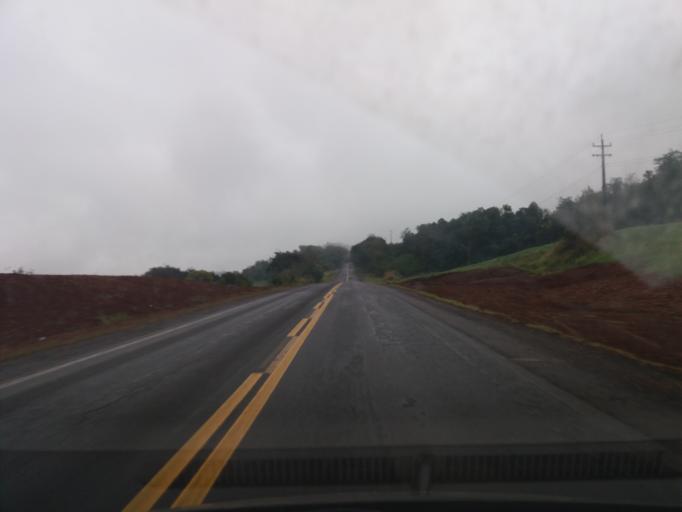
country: BR
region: Parana
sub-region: Ampere
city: Ampere
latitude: -25.8653
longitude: -53.4906
